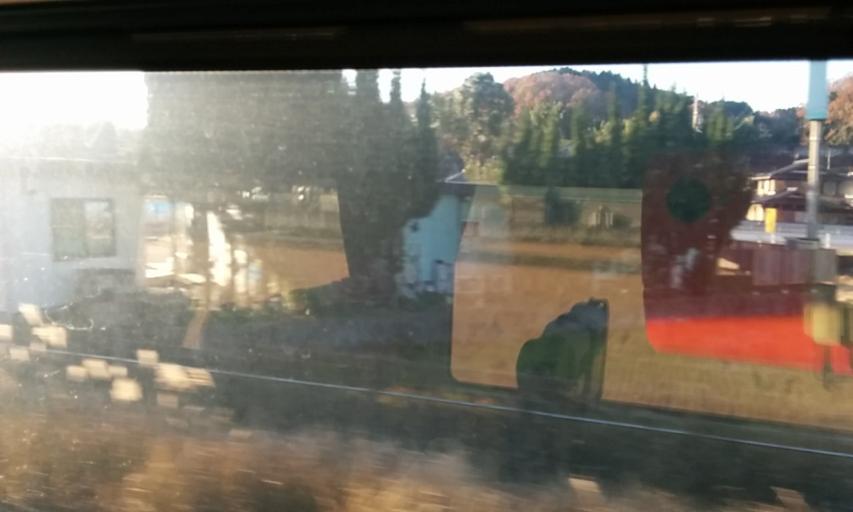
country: JP
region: Gifu
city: Mizunami
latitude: 35.3776
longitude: 137.2632
